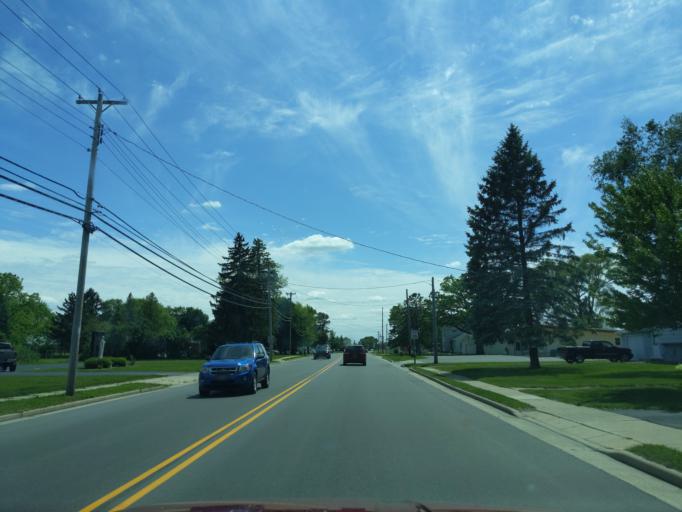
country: US
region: Wisconsin
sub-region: Columbia County
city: Pardeeville
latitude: 43.5305
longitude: -89.3023
